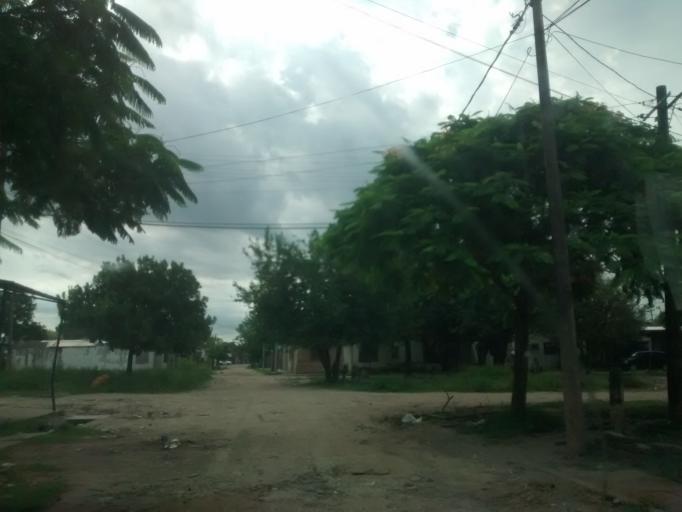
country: AR
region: Chaco
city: Resistencia
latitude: -27.4251
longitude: -58.9757
